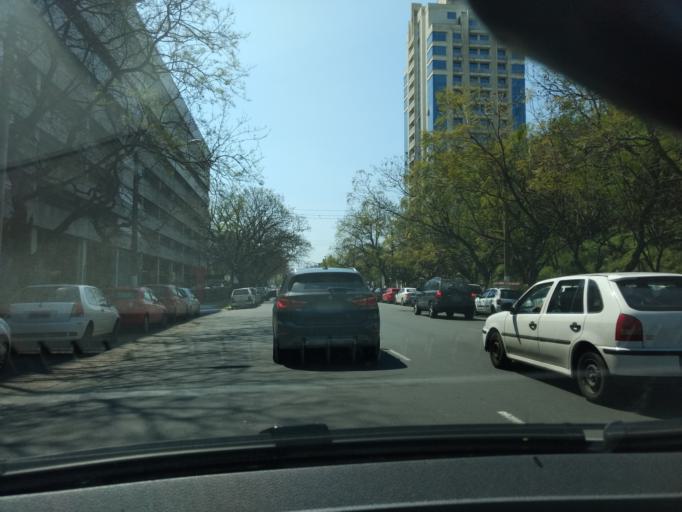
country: BR
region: Rio Grande do Sul
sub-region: Porto Alegre
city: Porto Alegre
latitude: -30.0243
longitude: -51.1613
